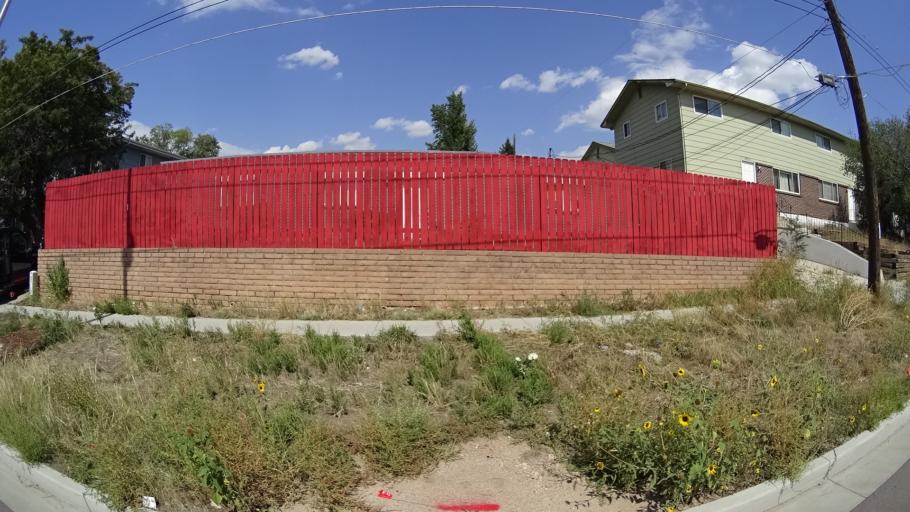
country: US
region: Colorado
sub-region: El Paso County
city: Stratmoor
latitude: 38.8254
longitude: -104.7665
